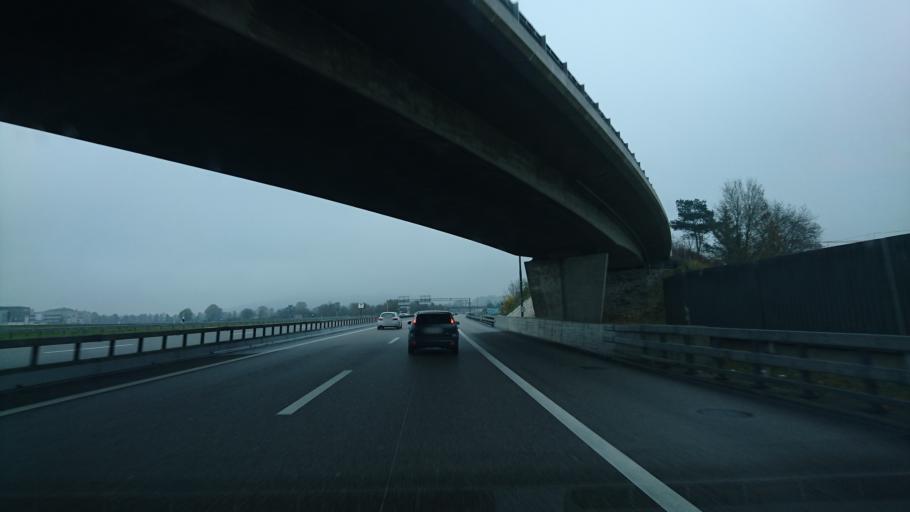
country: CH
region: Solothurn
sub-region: Bezirk Olten
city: Gunzgen
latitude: 47.3121
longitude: 7.8084
